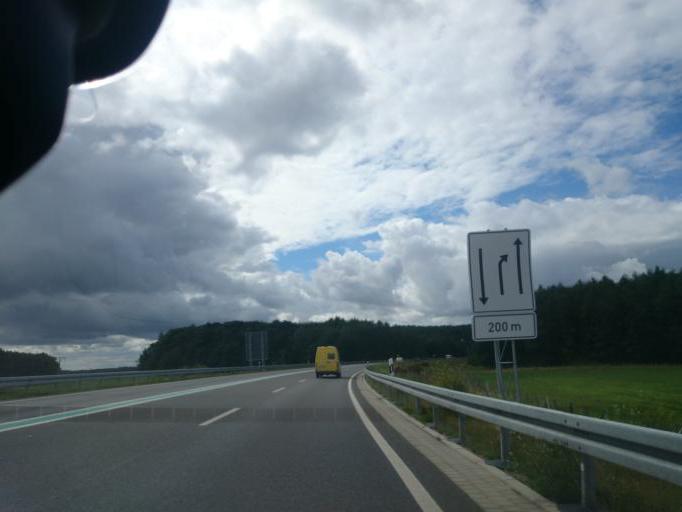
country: DE
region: Mecklenburg-Vorpommern
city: Samtens
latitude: 54.3594
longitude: 13.3109
